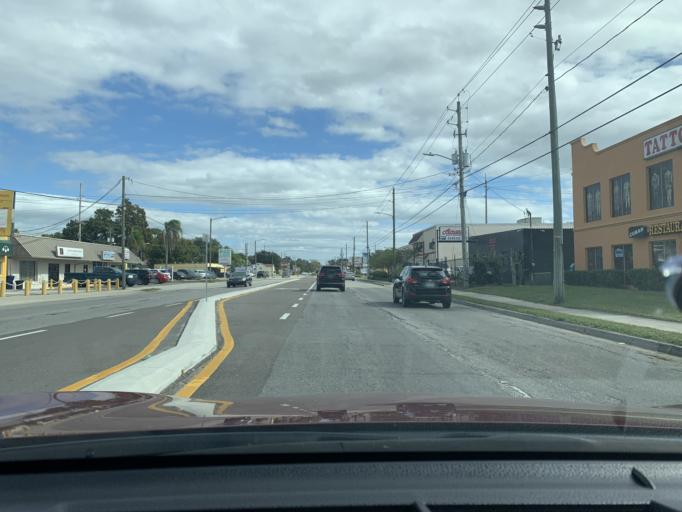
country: US
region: Florida
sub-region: Hillsborough County
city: Tampa
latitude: 27.9667
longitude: -82.5005
